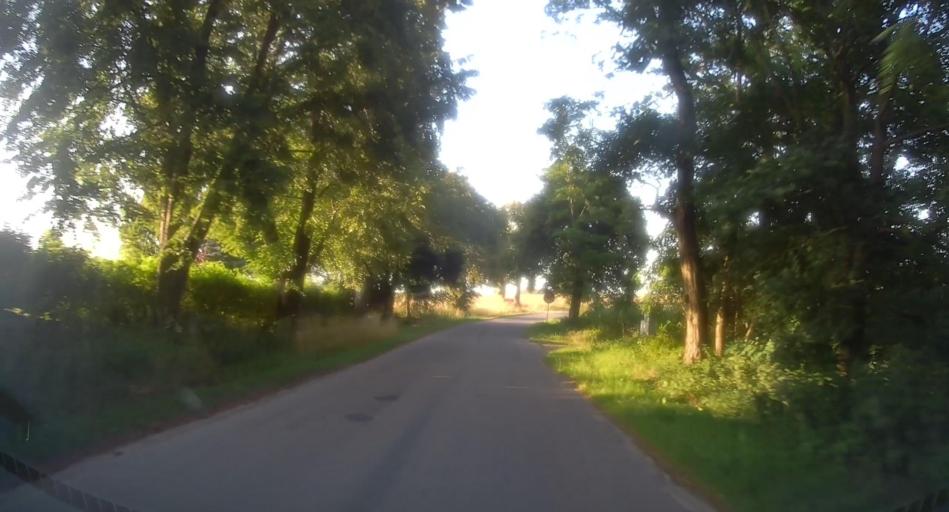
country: PL
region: Lodz Voivodeship
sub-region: Powiat skierniewicki
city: Kaweczyn Nowy
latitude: 51.8837
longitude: 20.2795
